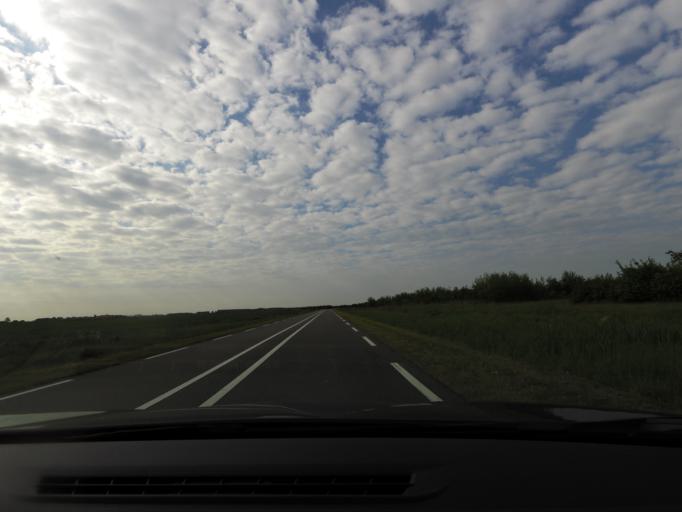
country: NL
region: Zeeland
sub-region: Schouwen-Duiveland
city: Renesse
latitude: 51.7197
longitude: 3.7778
